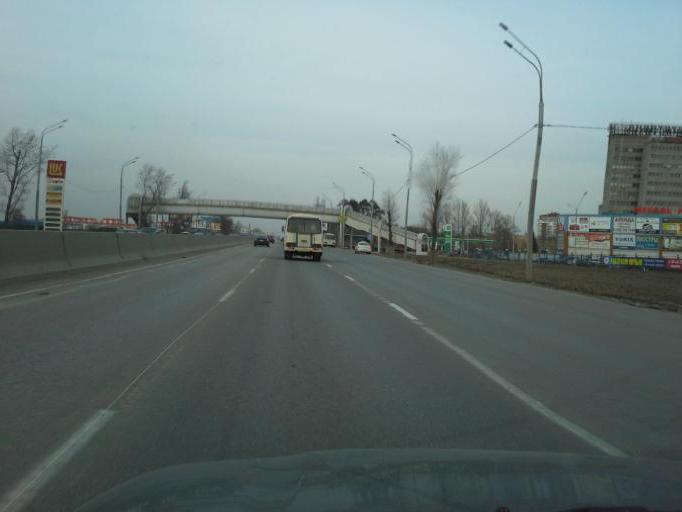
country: RU
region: Moskovskaya
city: Novoivanovskoye
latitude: 55.7038
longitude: 37.3537
